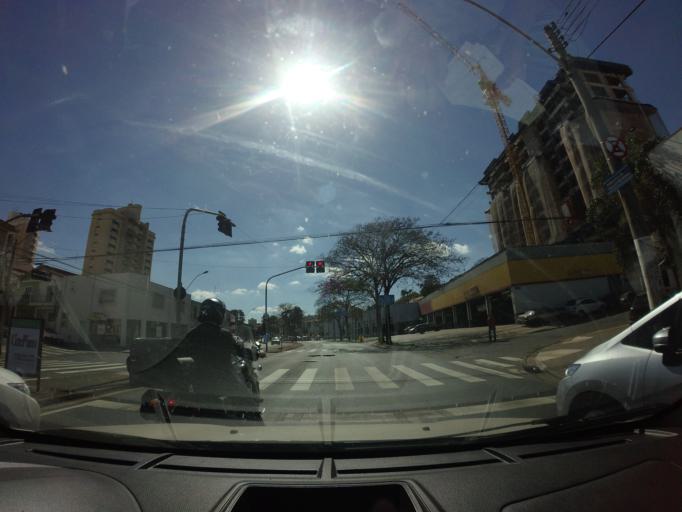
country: BR
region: Sao Paulo
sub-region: Piracicaba
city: Piracicaba
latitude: -22.7232
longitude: -47.6449
